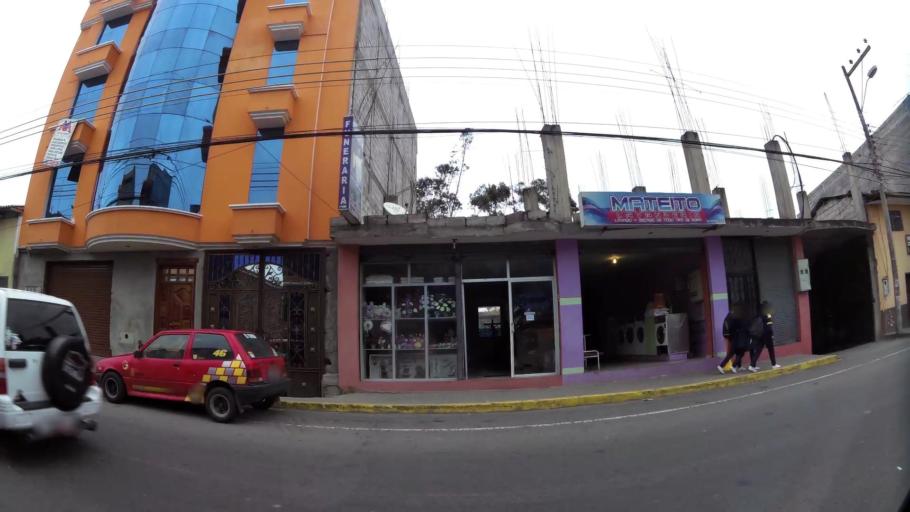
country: EC
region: Canar
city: Canar
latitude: -2.5115
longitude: -78.9295
